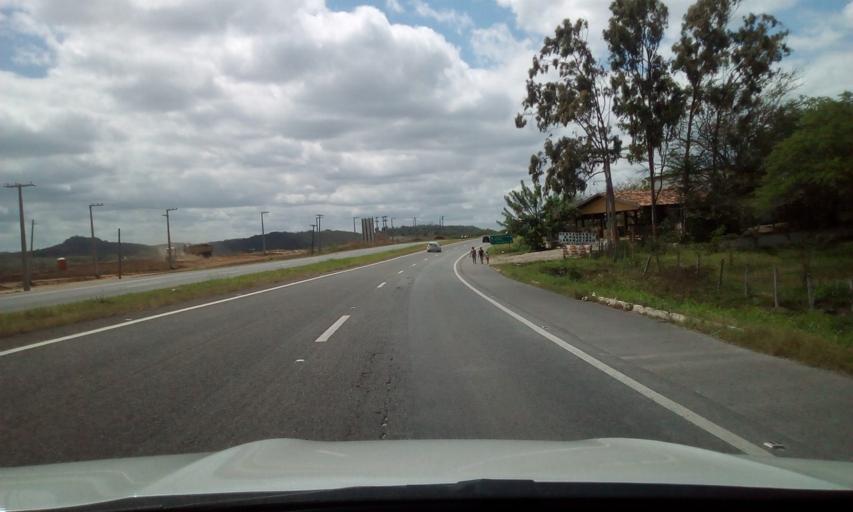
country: BR
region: Paraiba
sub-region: Massaranduba
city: Massaranduba
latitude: -7.2576
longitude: -35.8126
